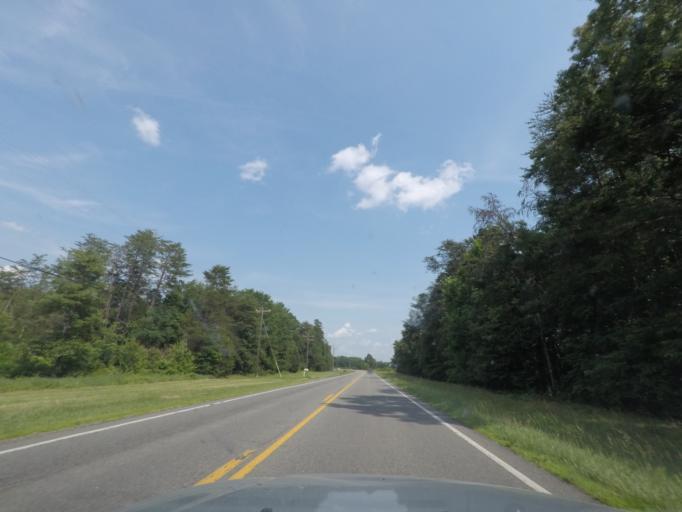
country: US
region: Virginia
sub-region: Fluvanna County
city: Palmyra
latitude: 37.8178
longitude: -78.2616
